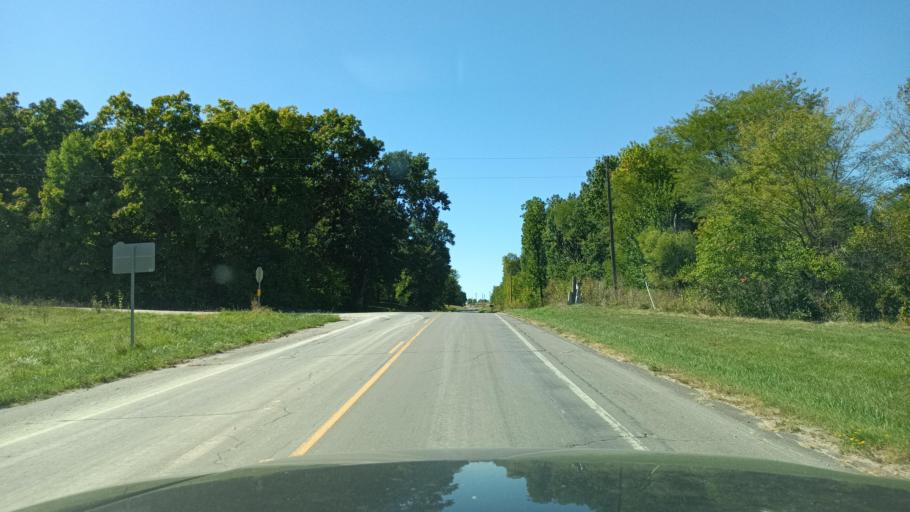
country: US
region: Missouri
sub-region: Macon County
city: La Plata
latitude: 40.0213
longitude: -92.5067
